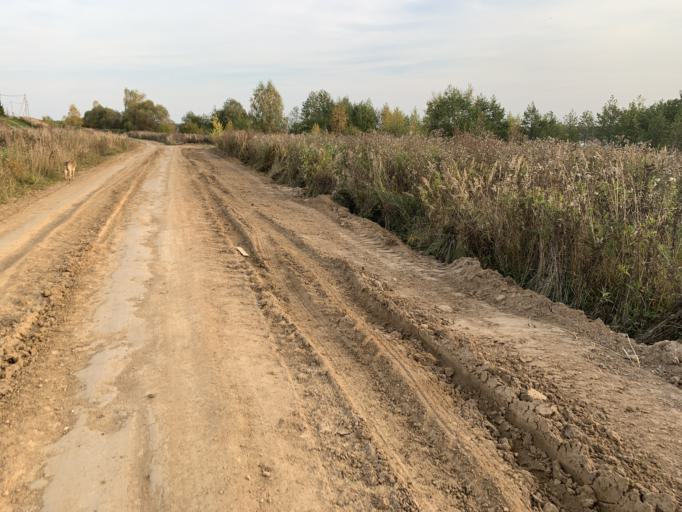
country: RU
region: Jaroslavl
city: Petrovsk
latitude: 56.9797
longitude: 39.3779
